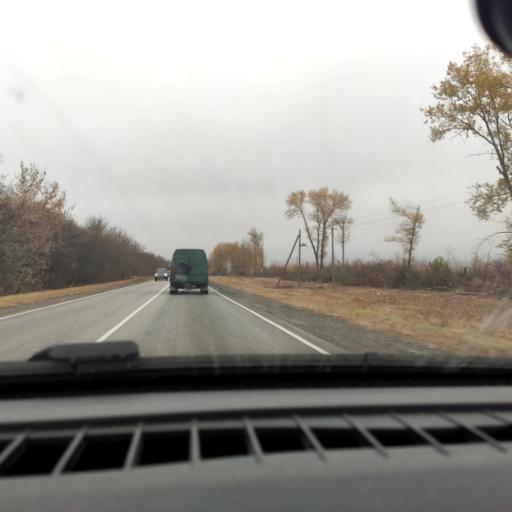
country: RU
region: Voronezj
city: Uryv-Pokrovka
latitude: 51.0835
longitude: 39.0015
